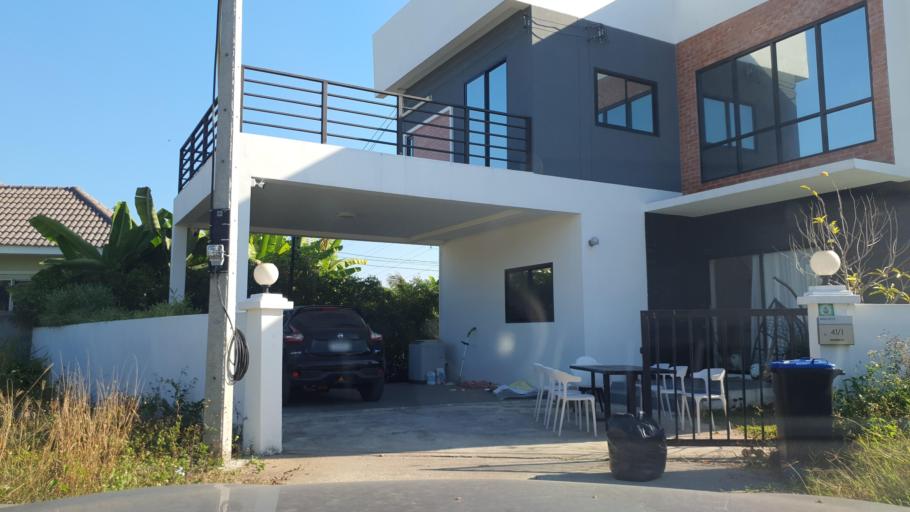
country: TH
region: Chiang Mai
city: Hang Dong
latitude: 18.6912
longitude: 98.9425
